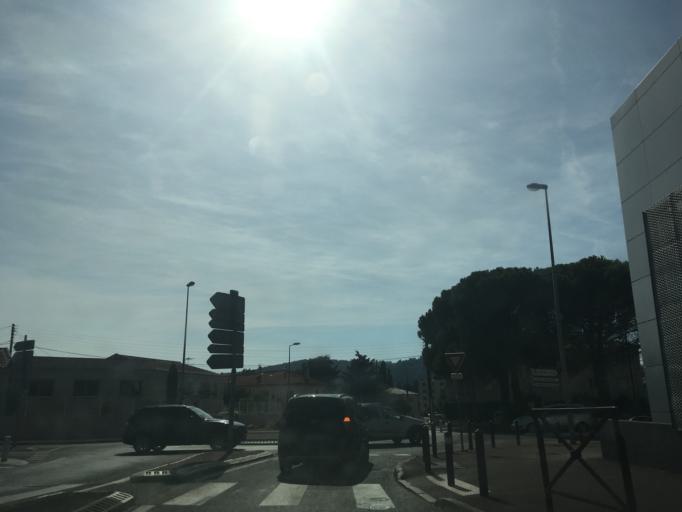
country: FR
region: Provence-Alpes-Cote d'Azur
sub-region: Departement du Var
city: Draguignan
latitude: 43.5318
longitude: 6.4741
